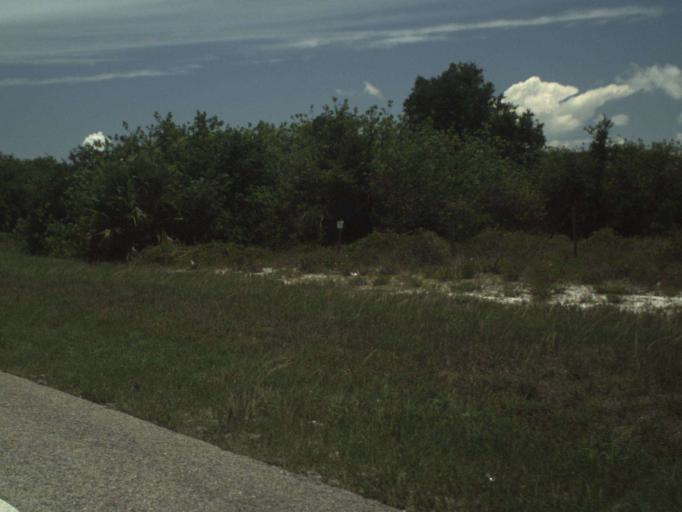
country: US
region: Florida
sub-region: Saint Lucie County
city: Lakewood Park
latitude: 27.5108
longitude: -80.3508
